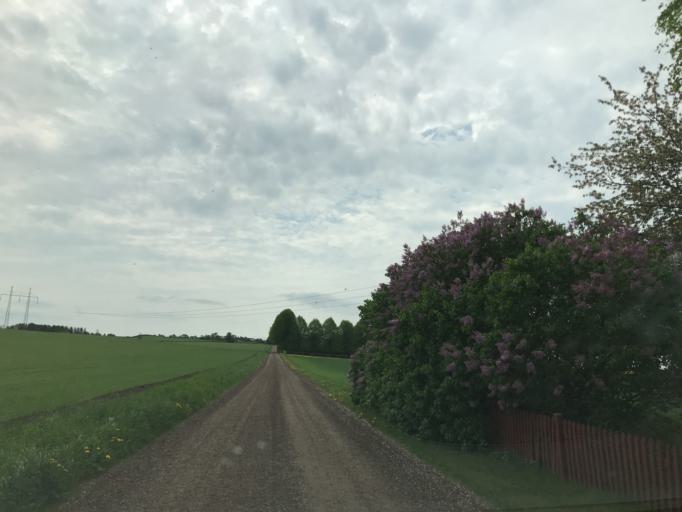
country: SE
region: Skane
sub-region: Svalovs Kommun
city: Teckomatorp
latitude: 55.8410
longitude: 13.0715
